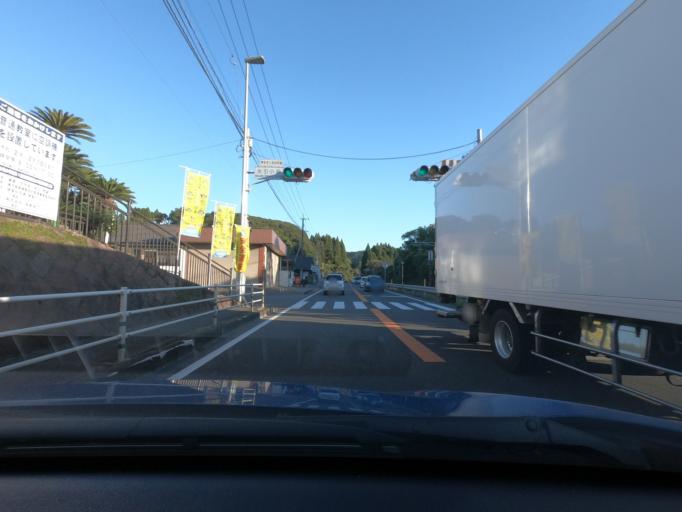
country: JP
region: Kagoshima
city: Satsumasendai
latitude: 31.8494
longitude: 130.2436
